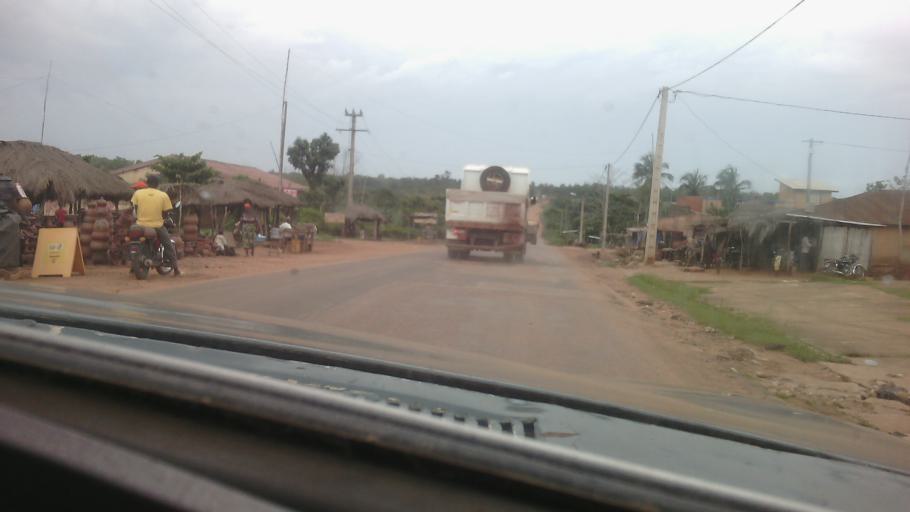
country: BJ
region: Mono
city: Come
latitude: 6.5087
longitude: 1.8296
